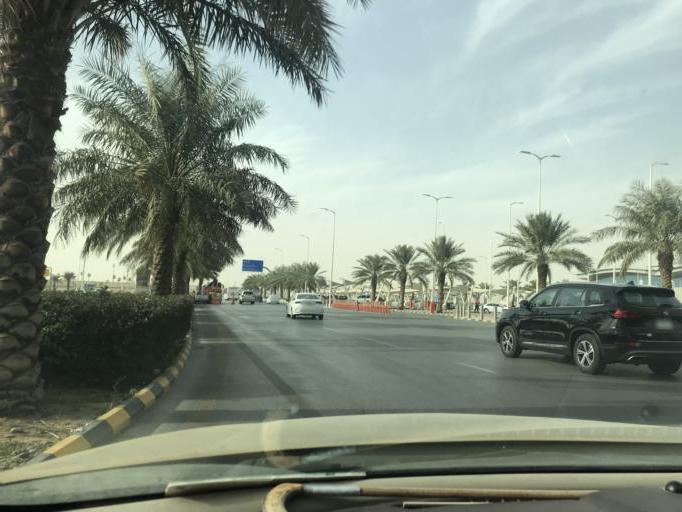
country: SA
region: Ar Riyad
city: Riyadh
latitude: 24.9428
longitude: 46.7104
